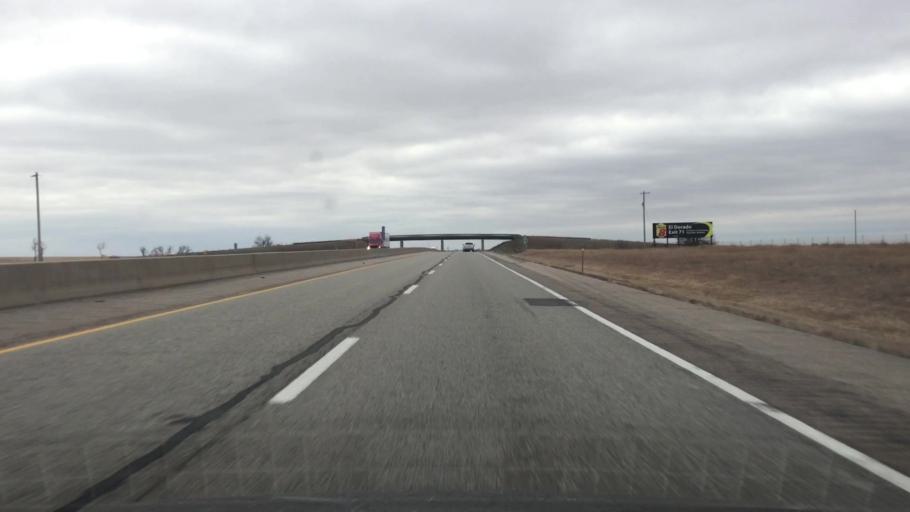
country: US
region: Kansas
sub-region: Butler County
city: El Dorado
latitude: 38.0004
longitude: -96.6905
